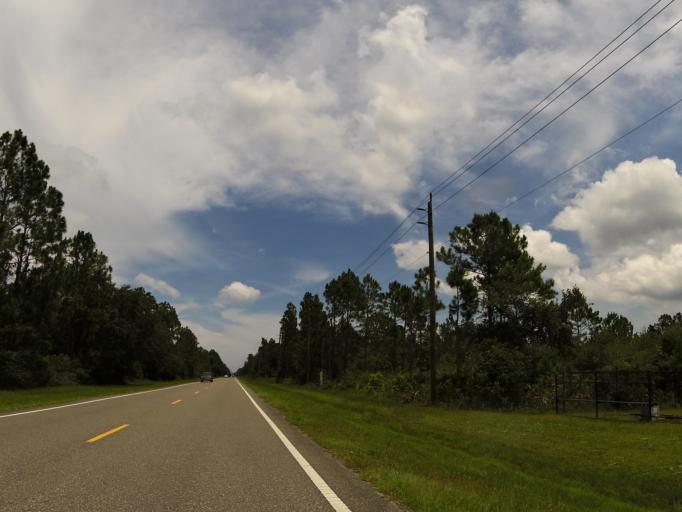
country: US
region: Florida
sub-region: Flagler County
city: Palm Coast
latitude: 29.6568
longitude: -81.3157
